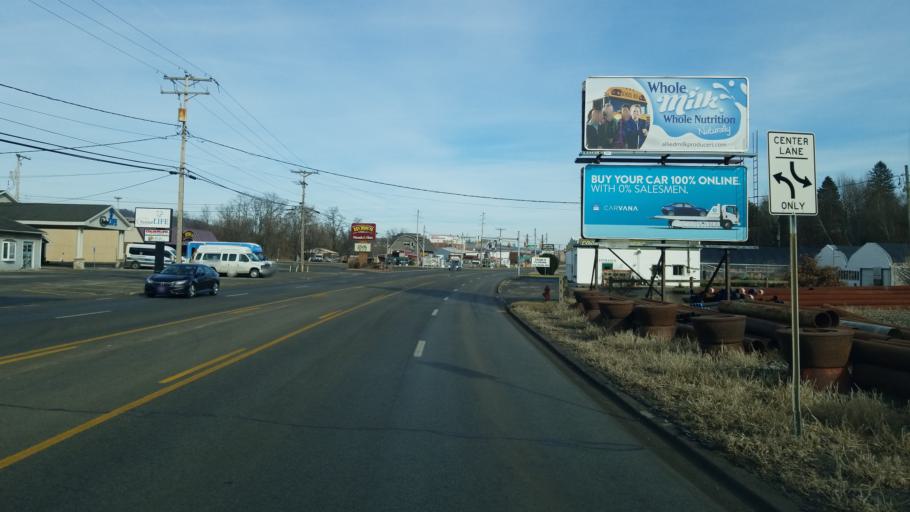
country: US
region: Pennsylvania
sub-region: Indiana County
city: Indiana
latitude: 40.6056
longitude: -79.1638
